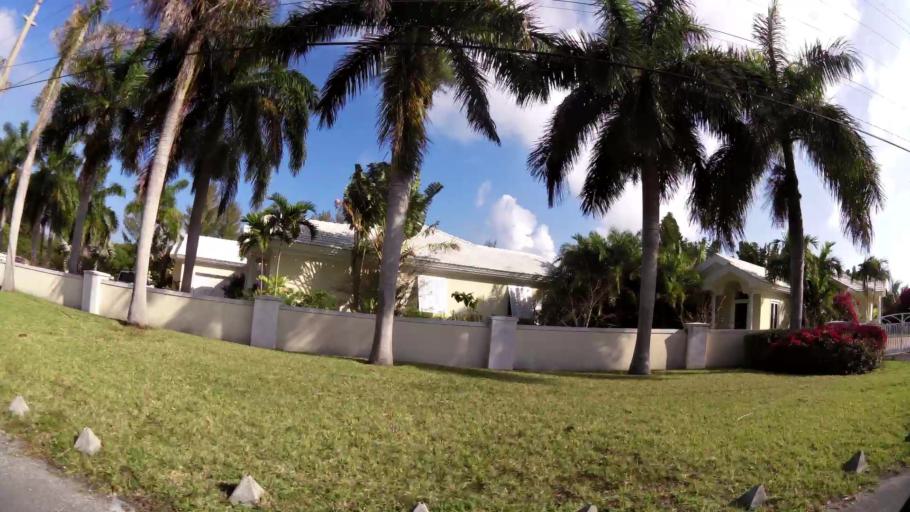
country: BS
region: Freeport
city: Lucaya
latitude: 26.5018
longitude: -78.6686
